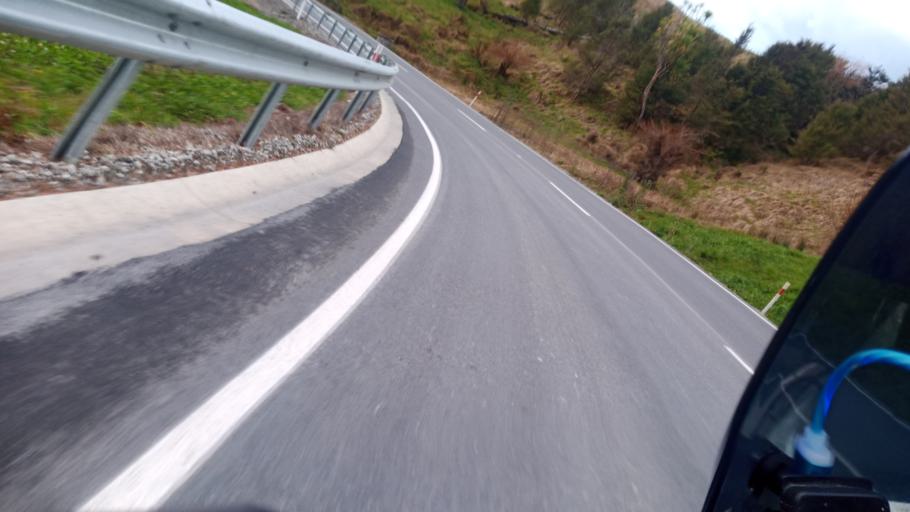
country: NZ
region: Gisborne
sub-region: Gisborne District
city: Gisborne
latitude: -38.0099
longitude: 178.2718
